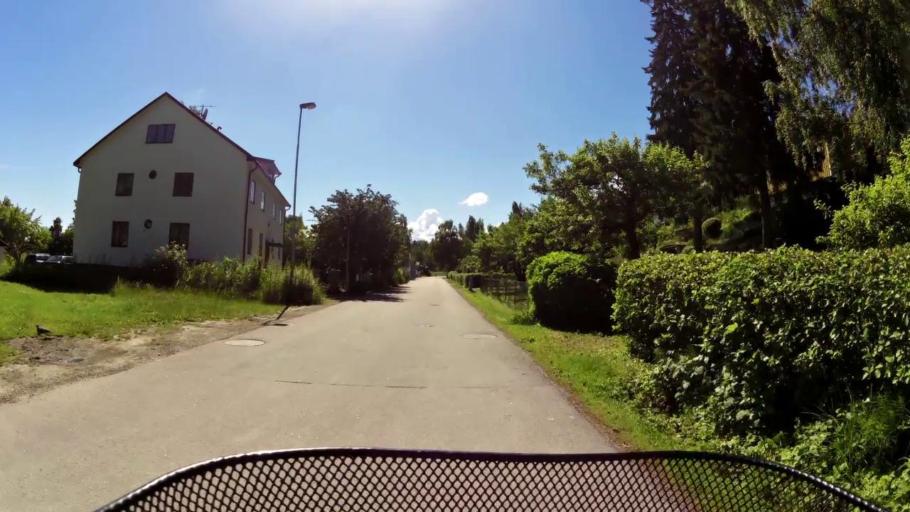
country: SE
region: OEstergoetland
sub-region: Linkopings Kommun
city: Sturefors
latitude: 58.3930
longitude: 15.6977
